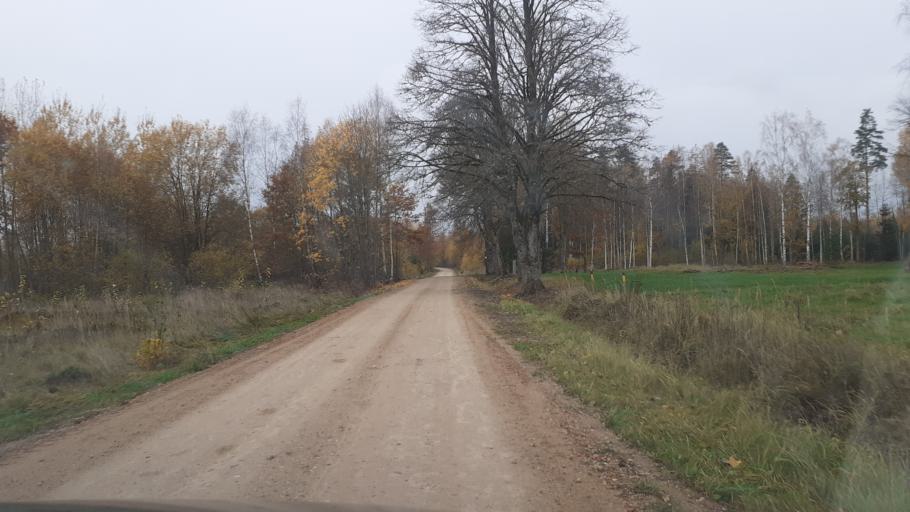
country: LV
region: Saldus Rajons
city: Saldus
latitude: 56.8755
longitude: 22.3135
